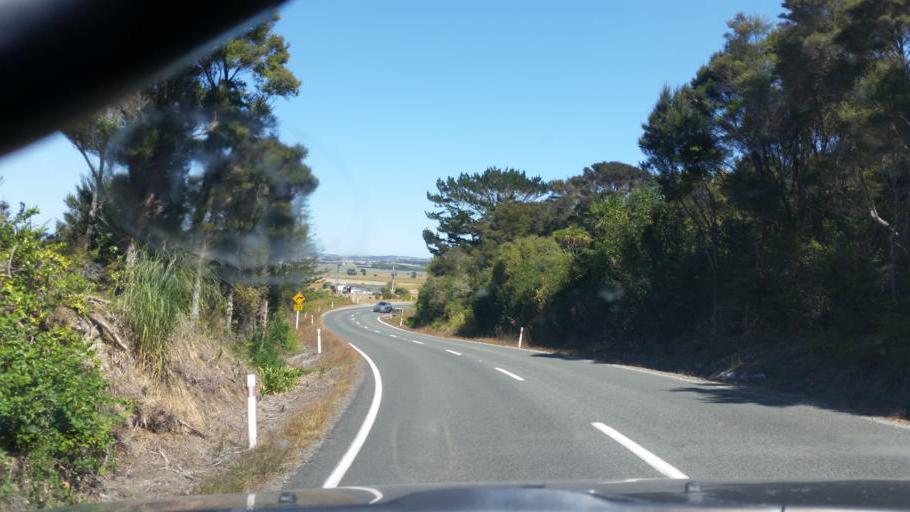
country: NZ
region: Northland
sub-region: Kaipara District
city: Dargaville
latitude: -36.0101
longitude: 173.9425
